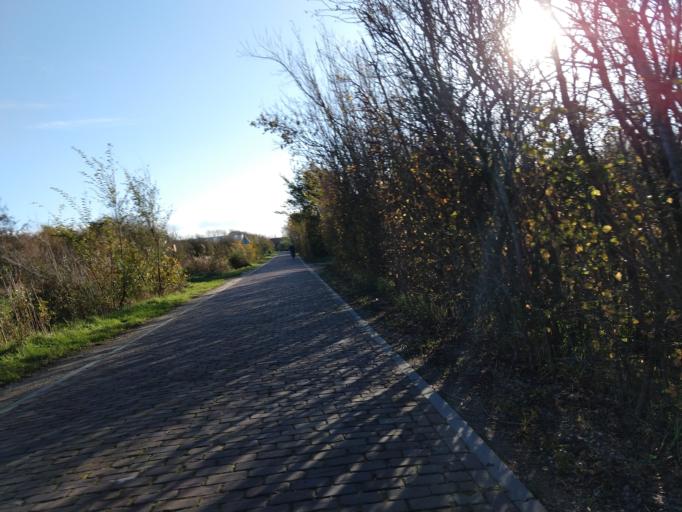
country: NL
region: Zeeland
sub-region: Gemeente Vlissingen
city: Vlissingen
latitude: 51.5068
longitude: 3.4836
